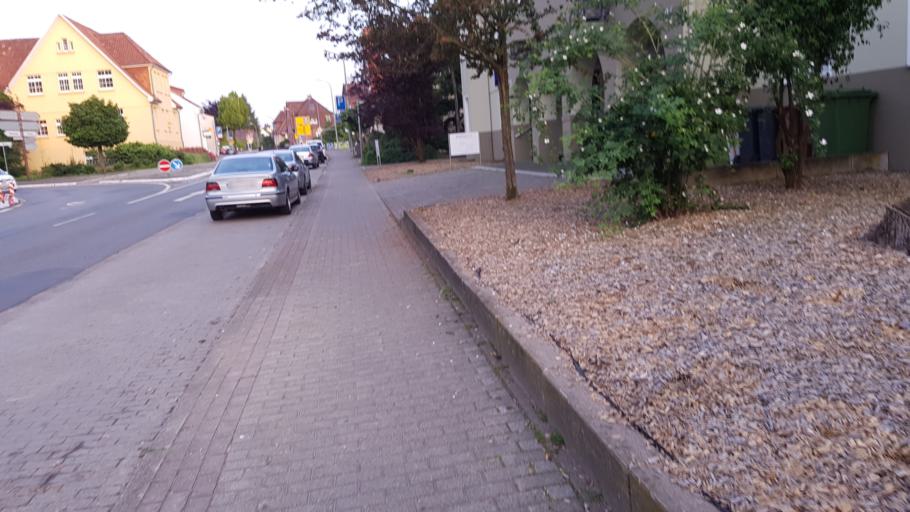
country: DE
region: Lower Saxony
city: Bomlitz
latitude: 52.9046
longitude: 9.6583
